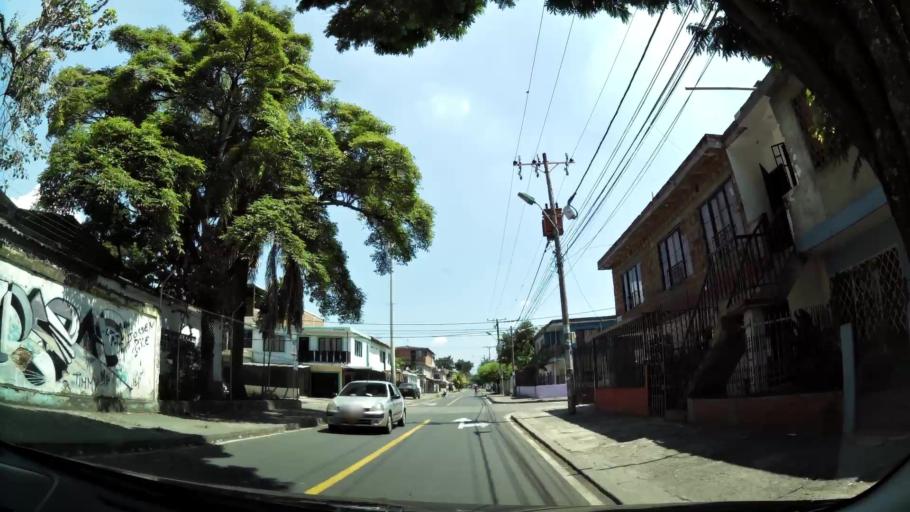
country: CO
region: Valle del Cauca
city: Cali
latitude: 3.4330
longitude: -76.4985
